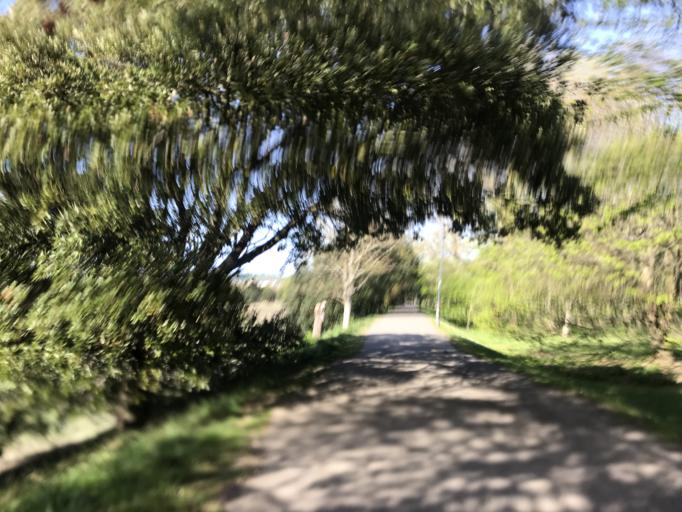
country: GB
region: England
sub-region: Devon
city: Barnstaple
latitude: 51.0693
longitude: -4.0558
